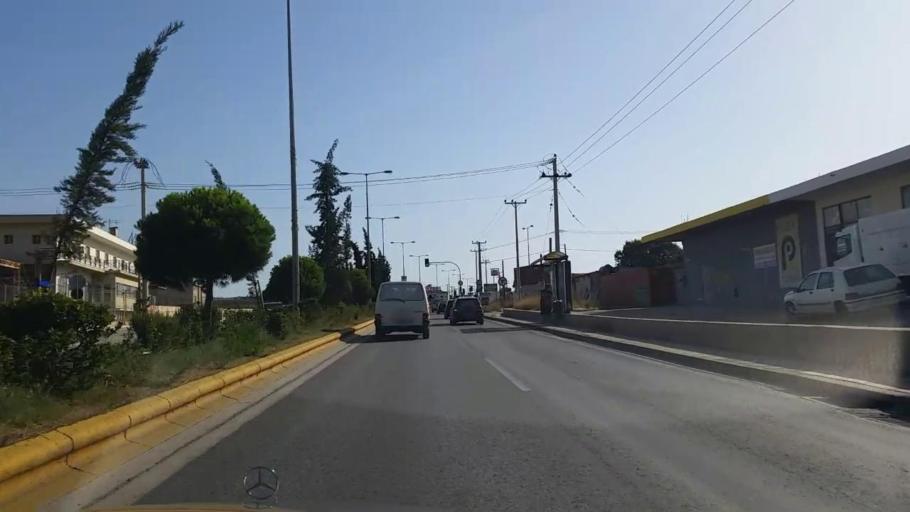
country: GR
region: Attica
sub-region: Nomarchia Anatolikis Attikis
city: Koropi
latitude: 37.8828
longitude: 23.8750
